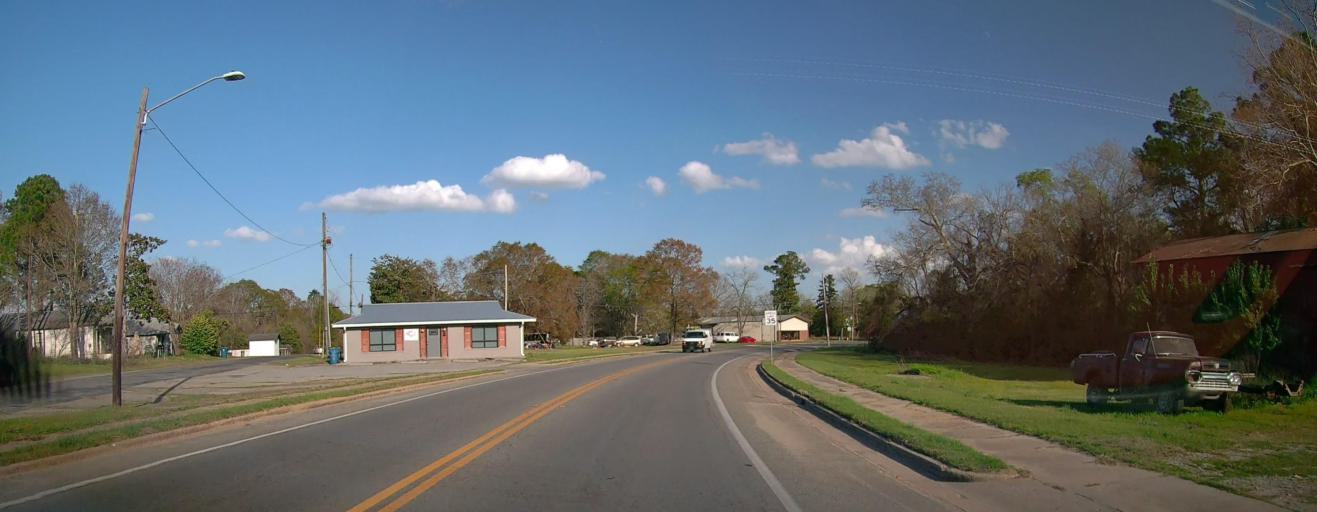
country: US
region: Georgia
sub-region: Toombs County
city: Lyons
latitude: 32.2030
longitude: -82.3197
